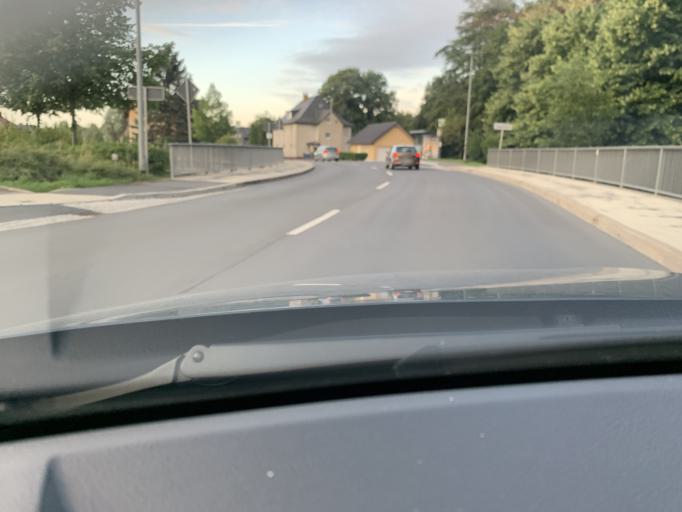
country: DE
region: Bavaria
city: Foritz
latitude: 50.3600
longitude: 11.2101
